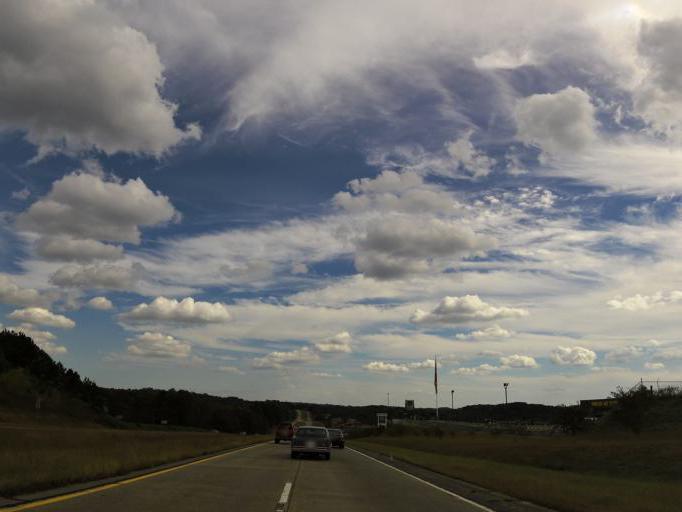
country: US
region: Georgia
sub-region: Pickens County
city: Nelson
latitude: 34.4051
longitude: -84.4207
